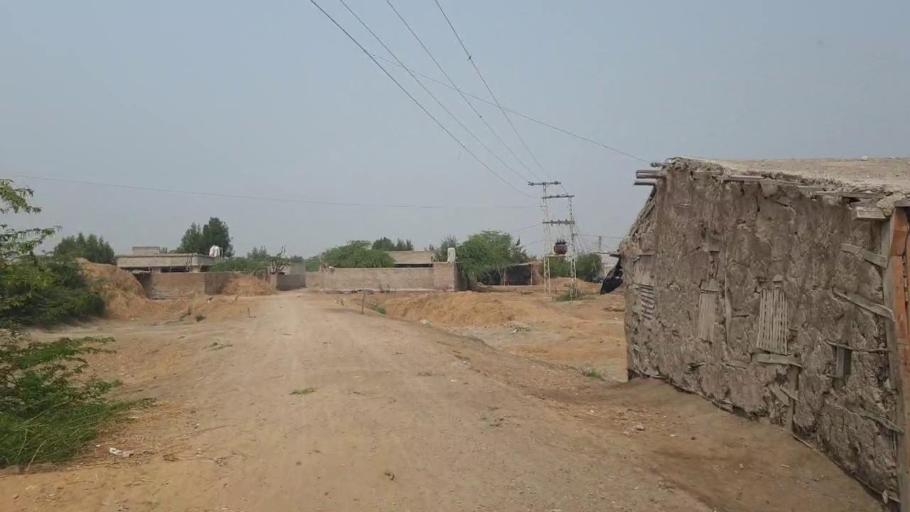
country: PK
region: Sindh
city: Kario
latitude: 24.6583
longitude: 68.6388
